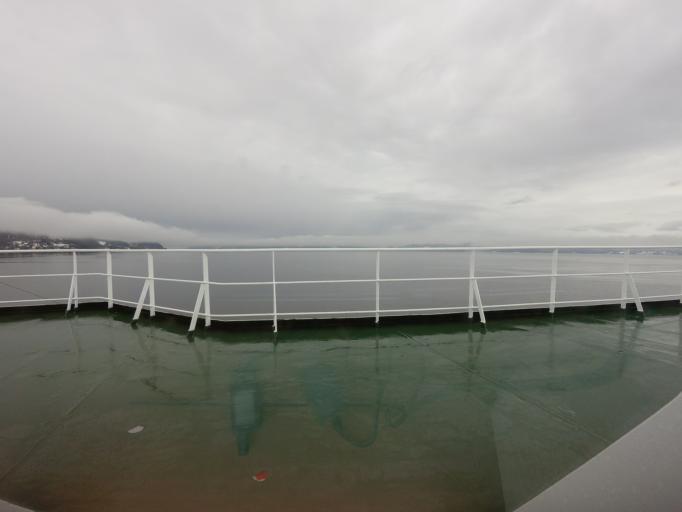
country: NO
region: Sor-Trondelag
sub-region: Trondheim
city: Trondheim
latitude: 63.4464
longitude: 10.3740
